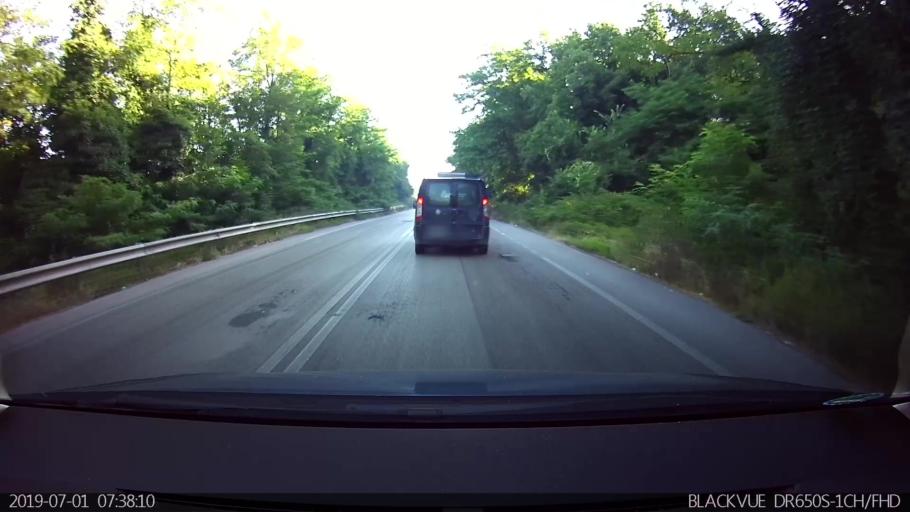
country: IT
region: Latium
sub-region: Provincia di Frosinone
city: Giuliano di Roma
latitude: 41.5422
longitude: 13.2682
